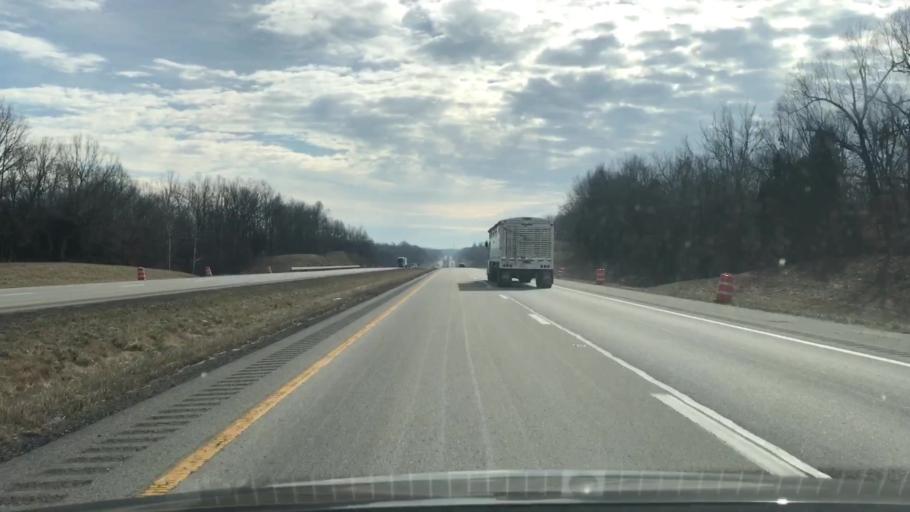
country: US
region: Kentucky
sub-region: Daviess County
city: Masonville
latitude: 37.5812
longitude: -86.9579
